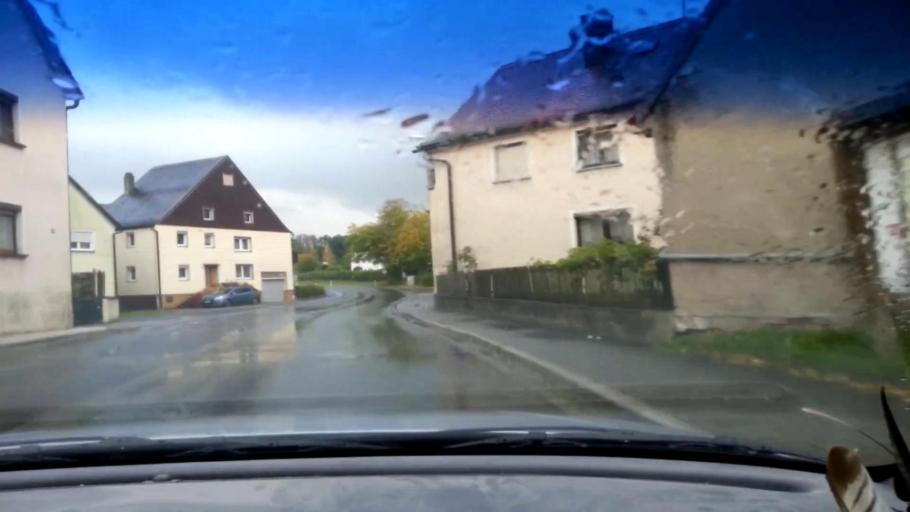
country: DE
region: Bavaria
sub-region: Upper Franconia
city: Burgebrach
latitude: 49.8451
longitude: 10.7303
